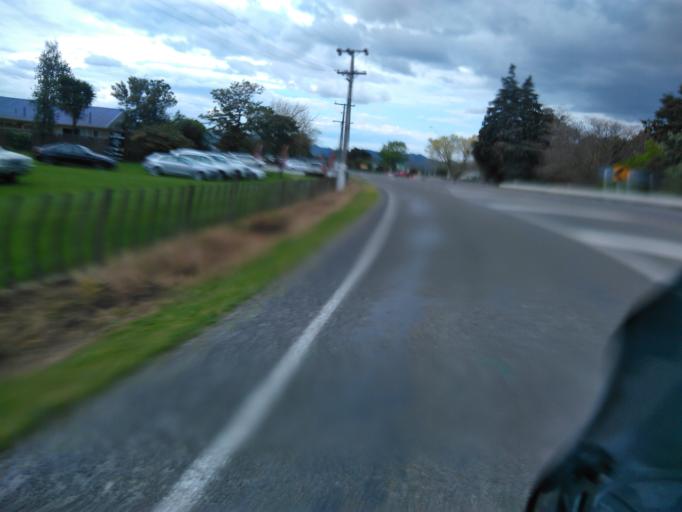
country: NZ
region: Gisborne
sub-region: Gisborne District
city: Gisborne
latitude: -38.6578
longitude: 177.9464
